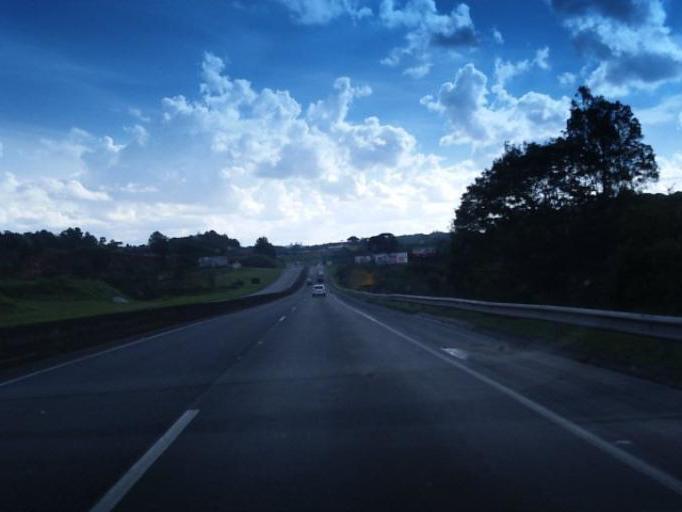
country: BR
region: Parana
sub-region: Campina Grande Do Sul
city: Campina Grande do Sul
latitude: -25.3383
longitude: -49.0377
